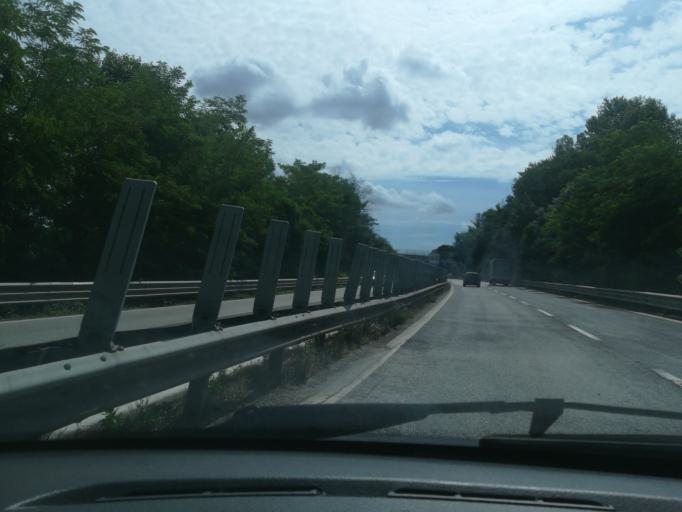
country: IT
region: The Marches
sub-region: Provincia di Macerata
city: Corridonia
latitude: 43.2649
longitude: 13.5299
